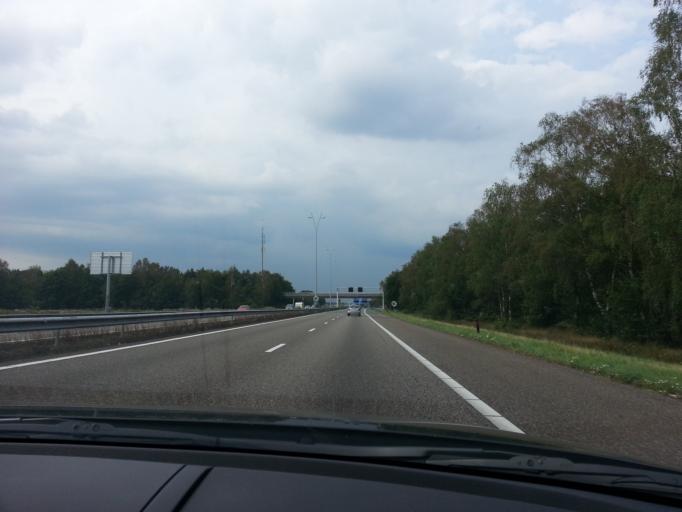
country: NL
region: North Brabant
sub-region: Gemeente Eindhoven
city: De Doornakkers
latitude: 51.3904
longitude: 5.5089
